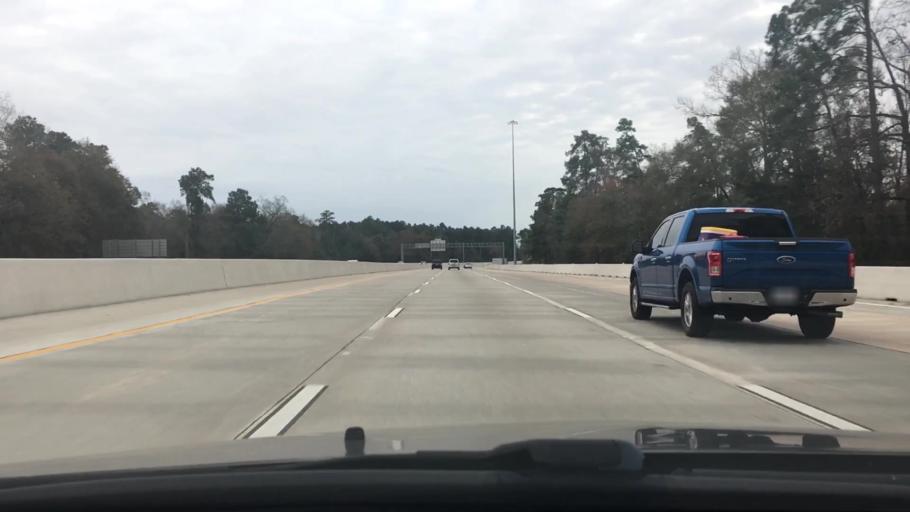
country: US
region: Texas
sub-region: Harris County
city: Spring
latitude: 30.0823
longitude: -95.4115
